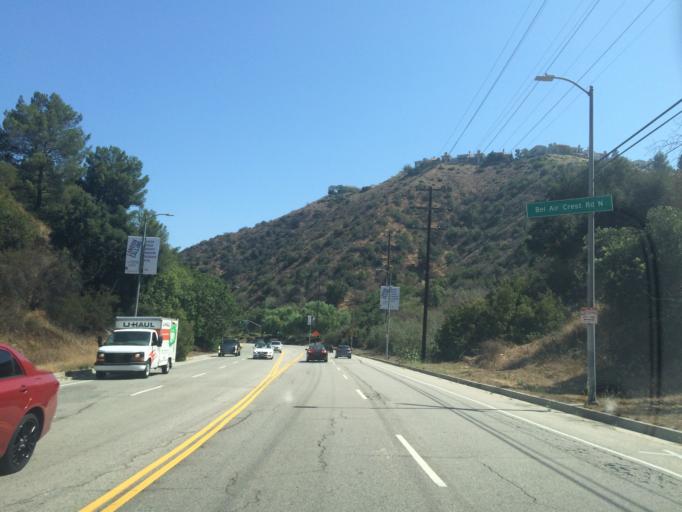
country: US
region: California
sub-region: Los Angeles County
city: Sherman Oaks
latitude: 34.1120
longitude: -118.4829
